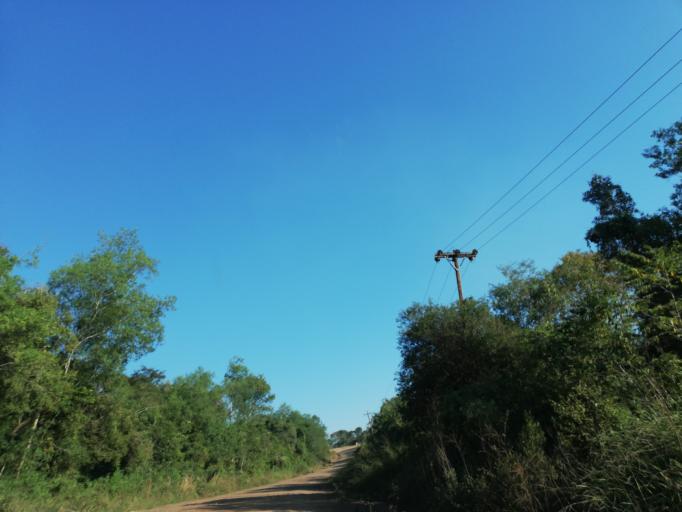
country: AR
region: Misiones
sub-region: Departamento de Candelaria
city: Candelaria
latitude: -27.5419
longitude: -55.7135
